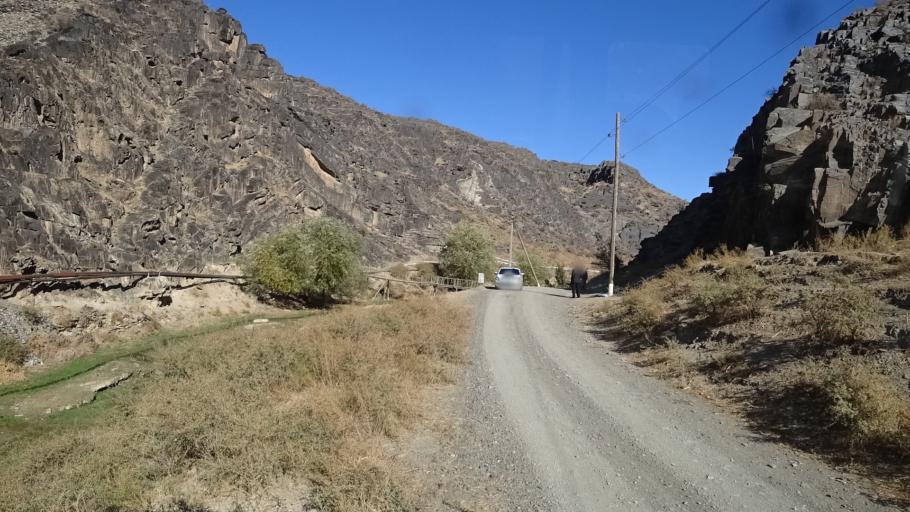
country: UZ
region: Navoiy
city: Nurota
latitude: 40.3053
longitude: 65.6173
